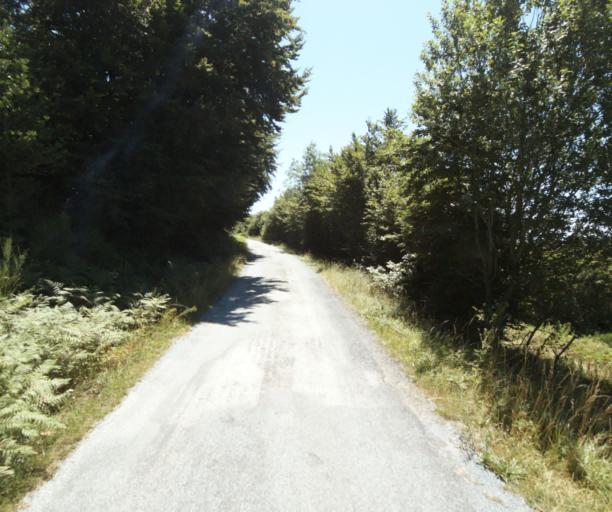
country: FR
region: Languedoc-Roussillon
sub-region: Departement de l'Aude
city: Cuxac-Cabardes
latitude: 43.4067
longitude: 2.2014
